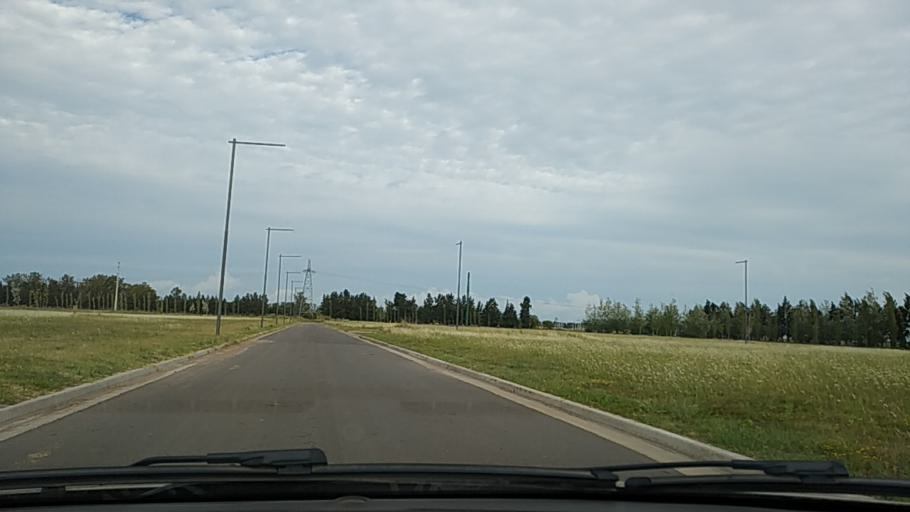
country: AR
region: Santa Fe
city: Perez
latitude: -32.9468
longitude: -60.7670
